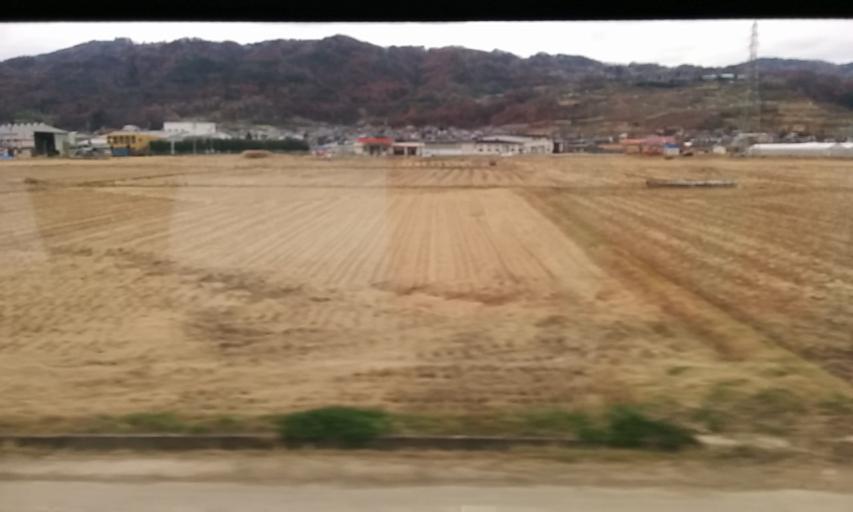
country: JP
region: Nagano
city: Nagano-shi
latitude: 36.5633
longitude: 138.1227
